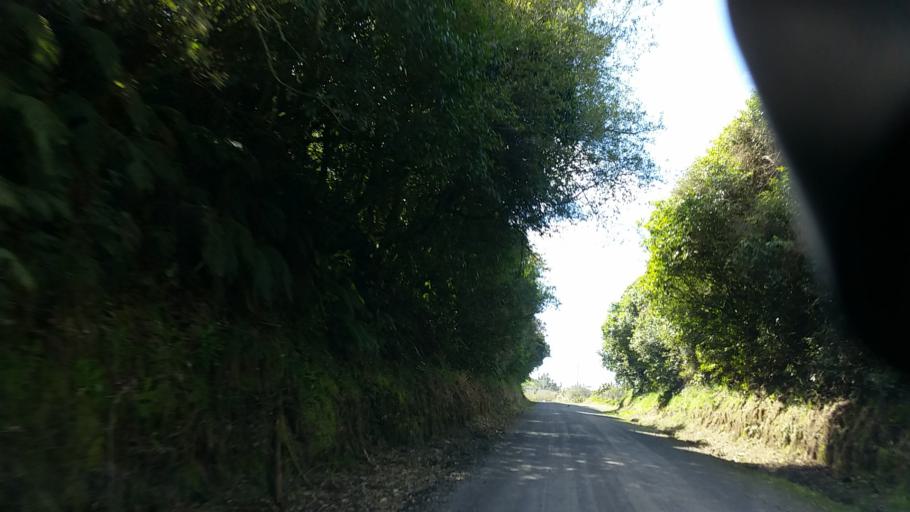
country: NZ
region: Waikato
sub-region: Taupo District
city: Taupo
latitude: -38.4849
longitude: 176.2112
